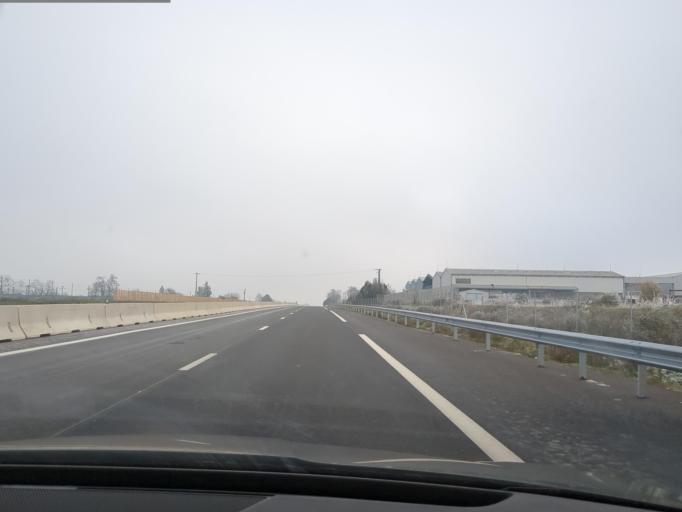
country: FR
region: Auvergne
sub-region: Departement de l'Allier
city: Lusigny
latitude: 46.5344
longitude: 3.5844
